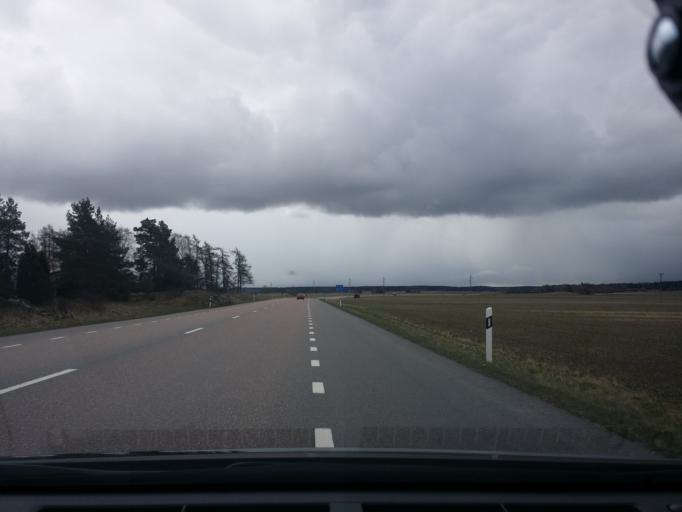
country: SE
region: Uppsala
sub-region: Enkopings Kommun
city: Irsta
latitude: 59.7555
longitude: 16.9346
